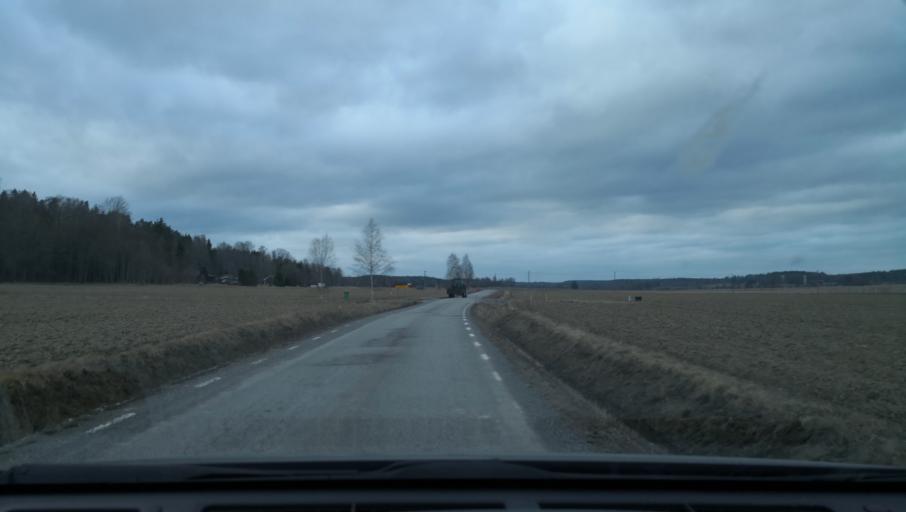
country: SE
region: Vaestmanland
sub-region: Kopings Kommun
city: Kolsva
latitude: 59.5531
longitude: 15.8753
